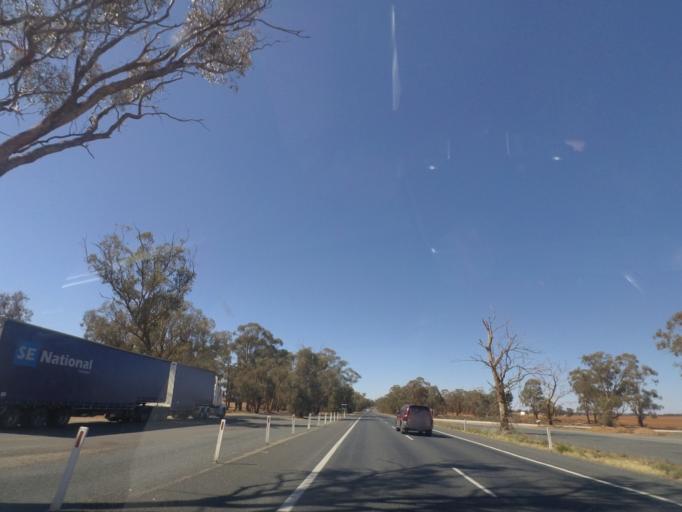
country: AU
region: New South Wales
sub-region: Bland
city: West Wyalong
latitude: -34.1994
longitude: 147.1105
